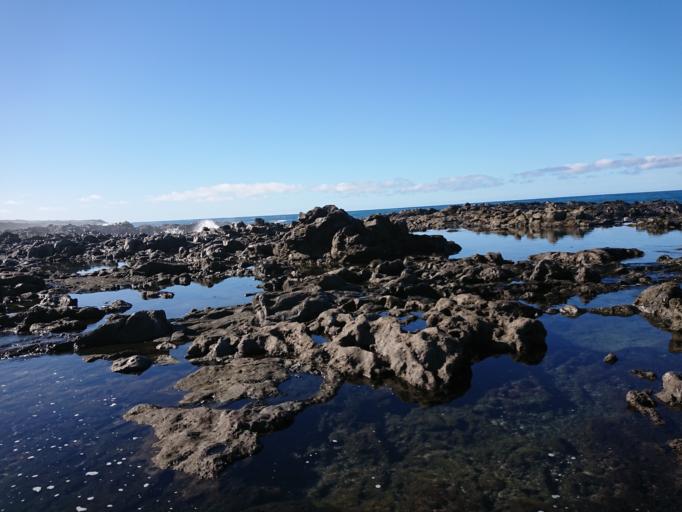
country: ES
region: Canary Islands
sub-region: Provincia de Las Palmas
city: Tinajo
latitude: 29.0835
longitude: -13.7253
